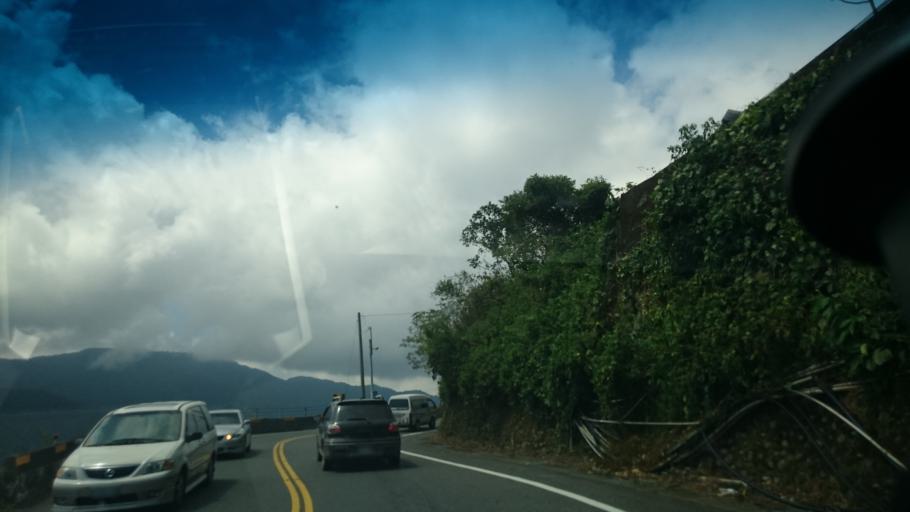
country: TW
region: Taiwan
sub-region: Nantou
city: Puli
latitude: 24.0391
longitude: 121.1450
